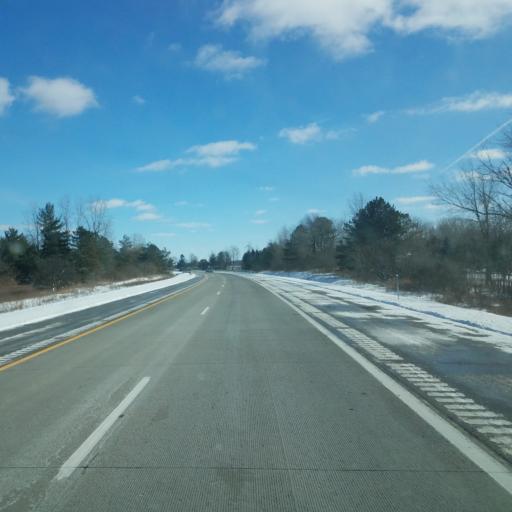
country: US
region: Michigan
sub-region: Ingham County
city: Okemos
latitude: 42.6742
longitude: -84.3928
